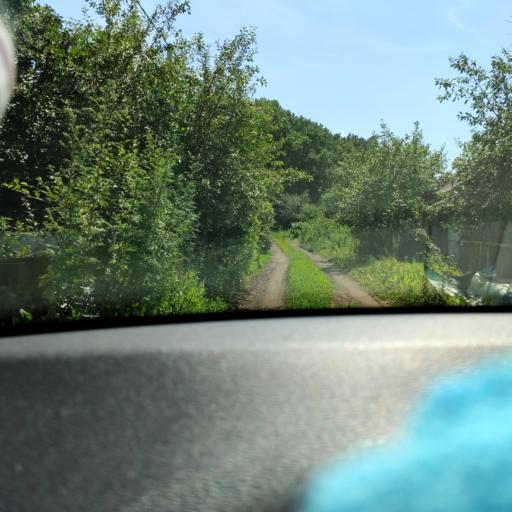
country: RU
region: Samara
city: Novosemeykino
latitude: 53.3301
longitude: 50.2559
